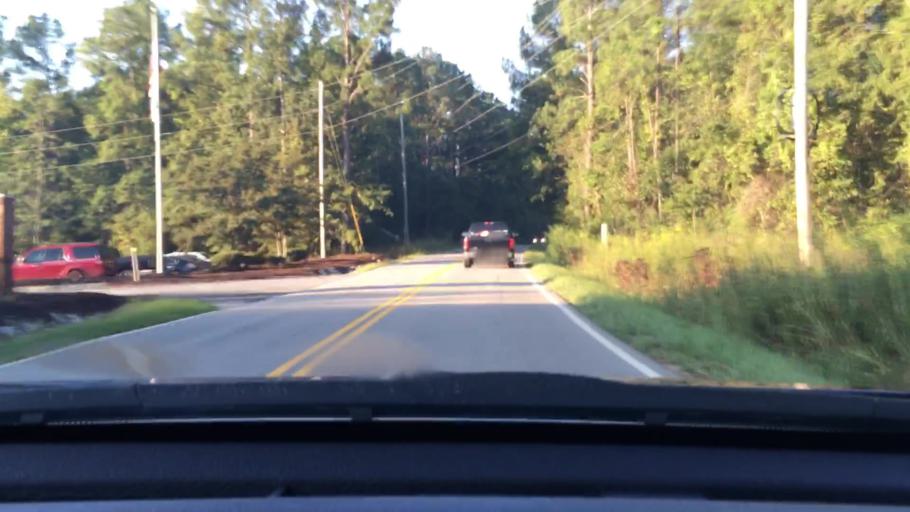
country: US
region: South Carolina
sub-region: Lexington County
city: Irmo
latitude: 34.0980
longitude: -81.1544
